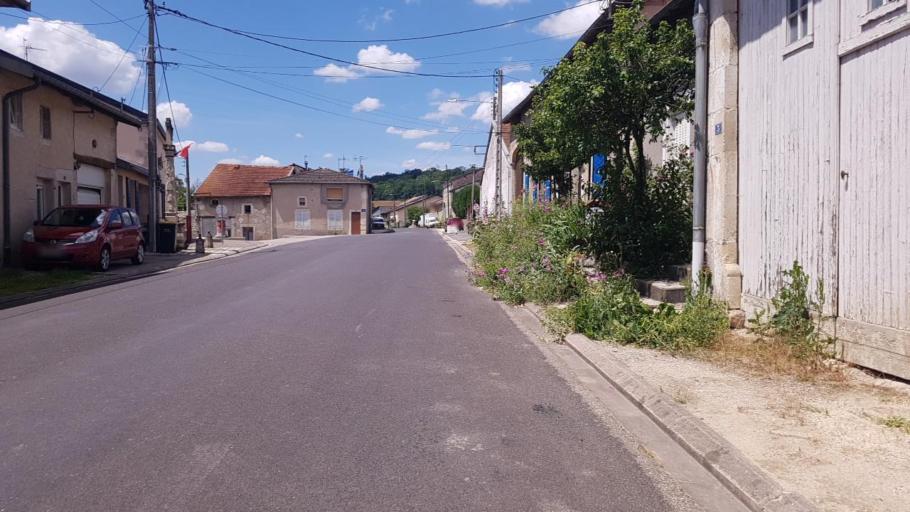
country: FR
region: Lorraine
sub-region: Departement de la Meuse
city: Ligny-en-Barrois
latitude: 48.6479
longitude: 5.4181
